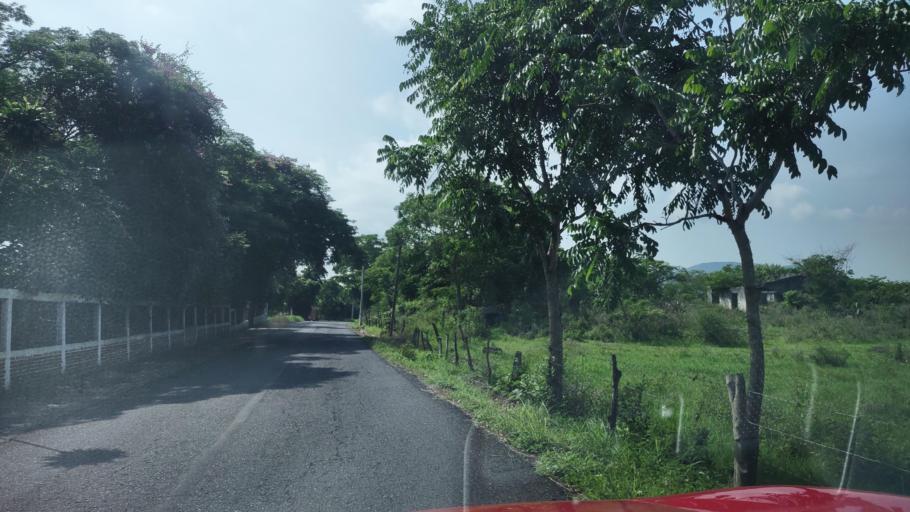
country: MX
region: Veracruz
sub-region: Coatepec
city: Bella Esperanza
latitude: 19.4524
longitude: -96.8299
